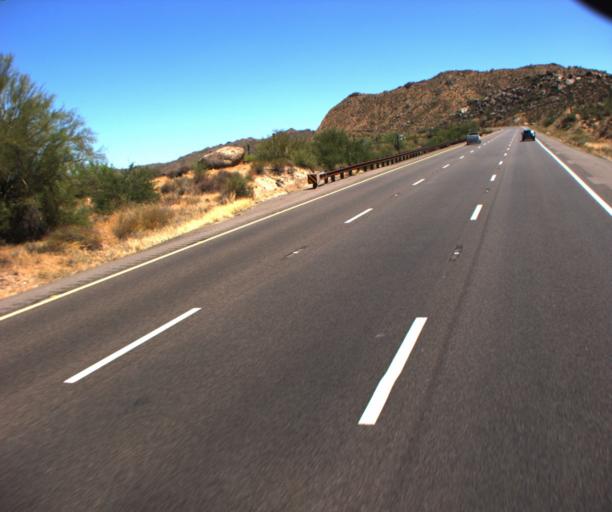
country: US
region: Arizona
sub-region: Maricopa County
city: Rio Verde
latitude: 33.7174
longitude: -111.5110
